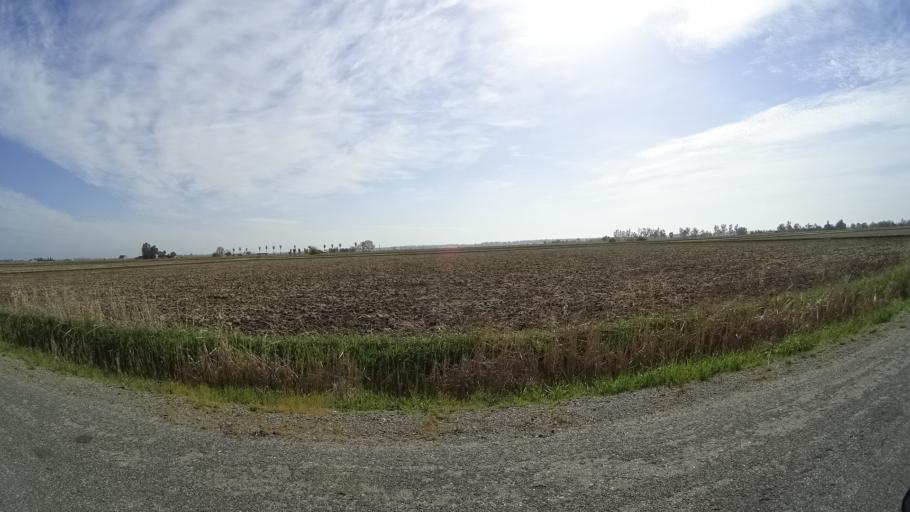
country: US
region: California
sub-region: Glenn County
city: Hamilton City
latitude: 39.5897
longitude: -122.0464
